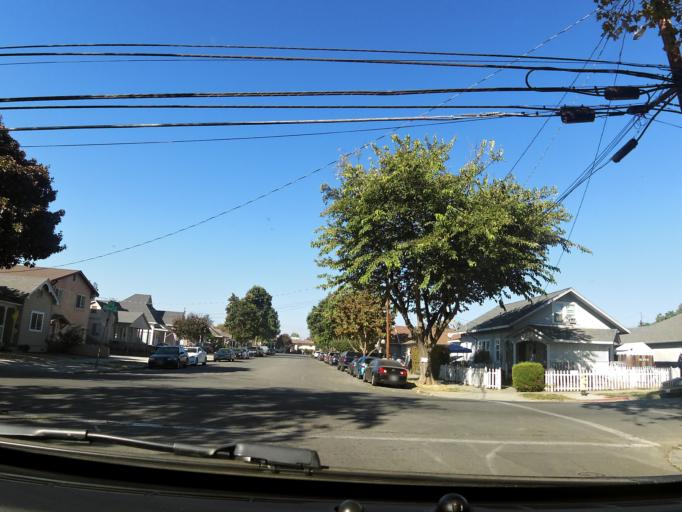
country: US
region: California
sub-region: San Benito County
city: Hollister
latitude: 36.8506
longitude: -121.4075
